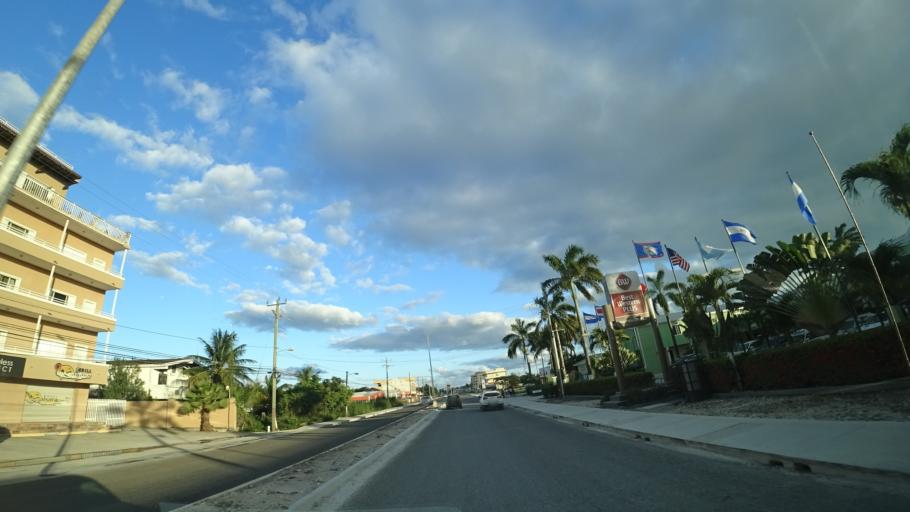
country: BZ
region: Belize
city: Belize City
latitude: 17.5148
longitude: -88.2246
